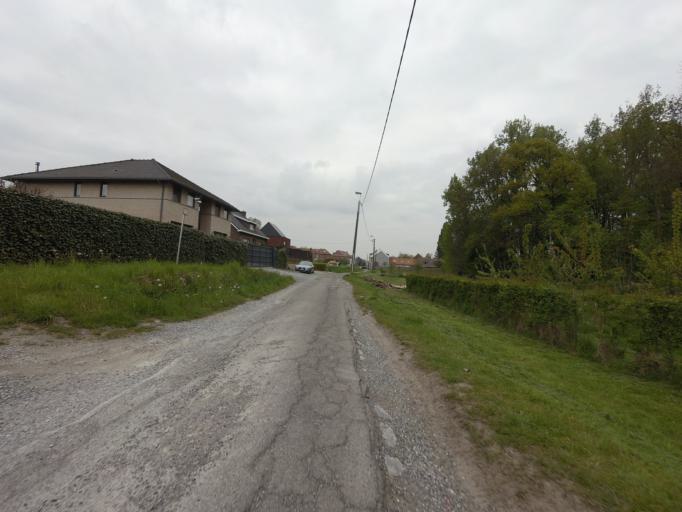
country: BE
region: Flanders
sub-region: Provincie Vlaams-Brabant
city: Grimbergen
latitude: 50.9091
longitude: 4.3797
